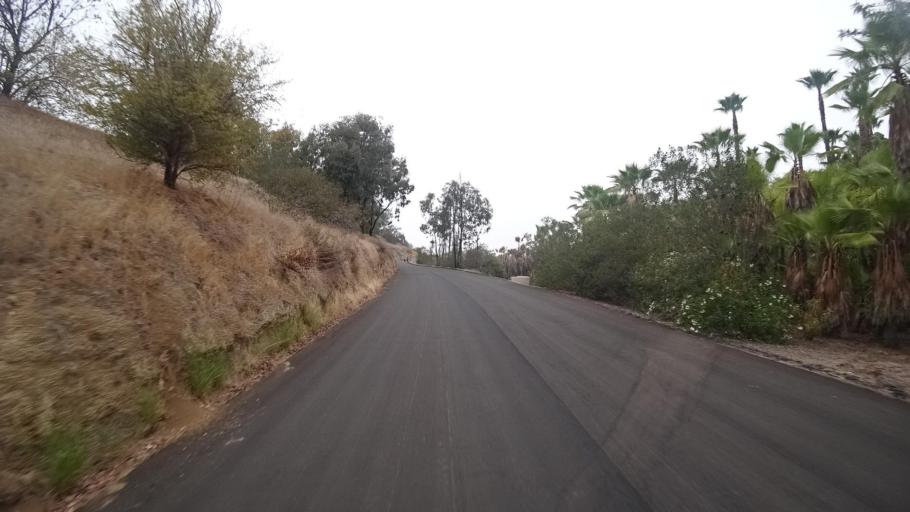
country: US
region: California
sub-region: San Diego County
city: Rainbow
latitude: 33.3773
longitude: -117.1753
